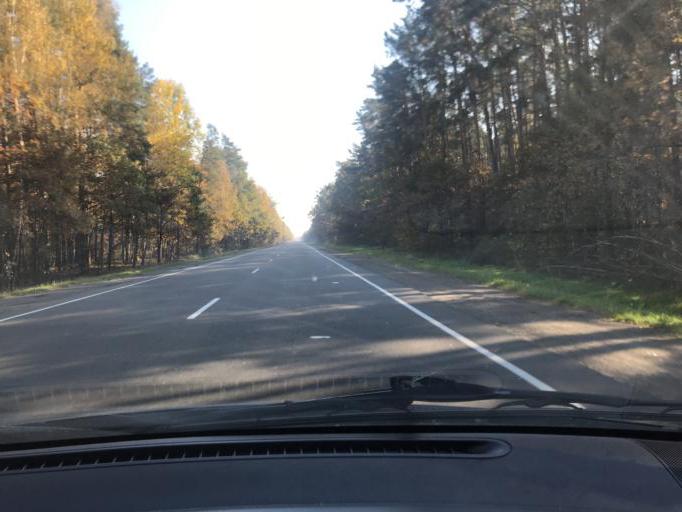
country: BY
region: Brest
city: Horad Luninyets
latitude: 52.2856
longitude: 26.8007
